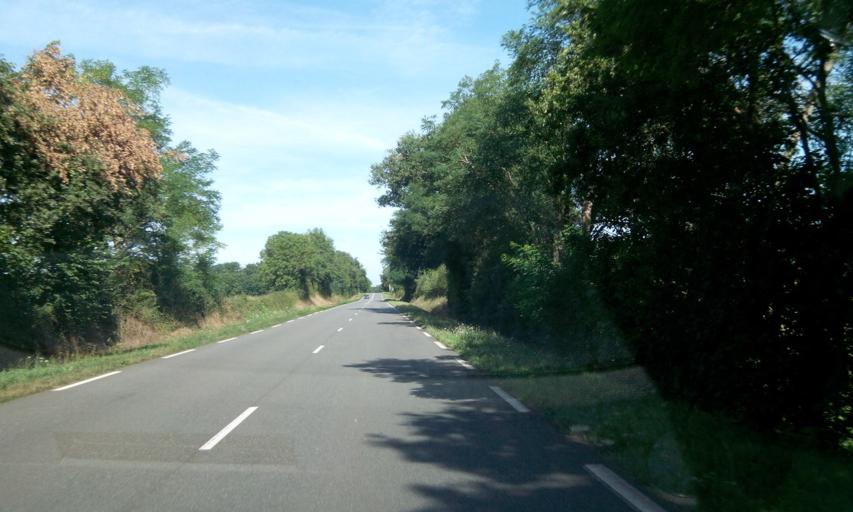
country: FR
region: Poitou-Charentes
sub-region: Departement de la Charente
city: Chabanais
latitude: 45.9479
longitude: 0.7206
